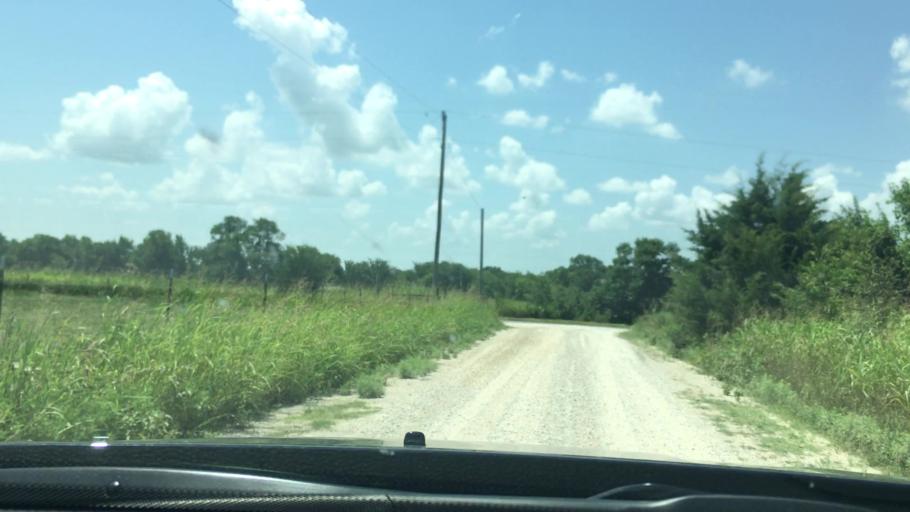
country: US
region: Oklahoma
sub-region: Pontotoc County
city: Ada
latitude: 34.6951
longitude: -96.5562
